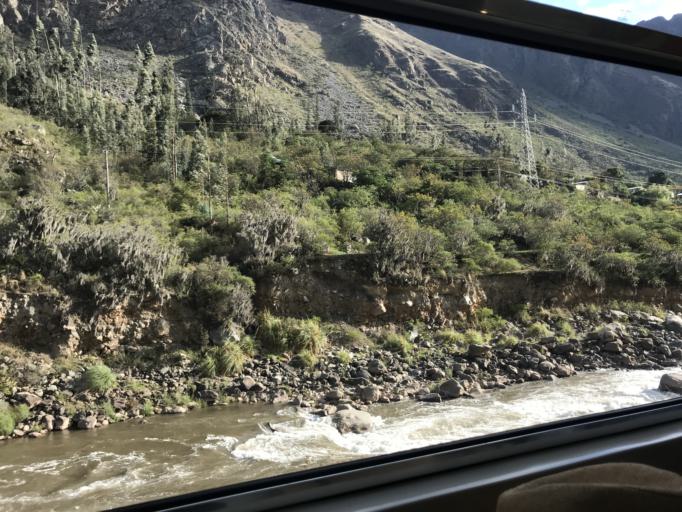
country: PE
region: Cusco
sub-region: Provincia de Urubamba
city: Ollantaytambo
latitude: -13.2266
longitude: -72.4009
